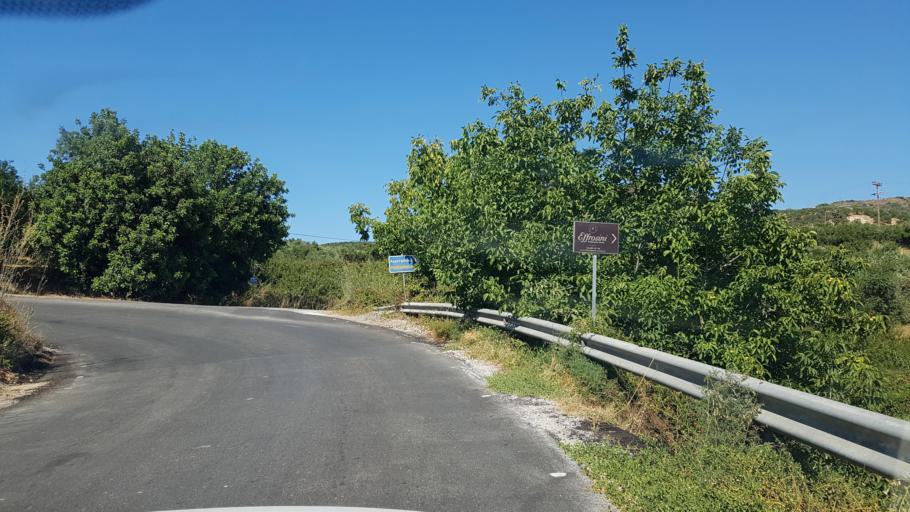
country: GR
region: Crete
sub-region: Nomos Chanias
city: Kissamos
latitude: 35.4954
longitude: 23.7214
